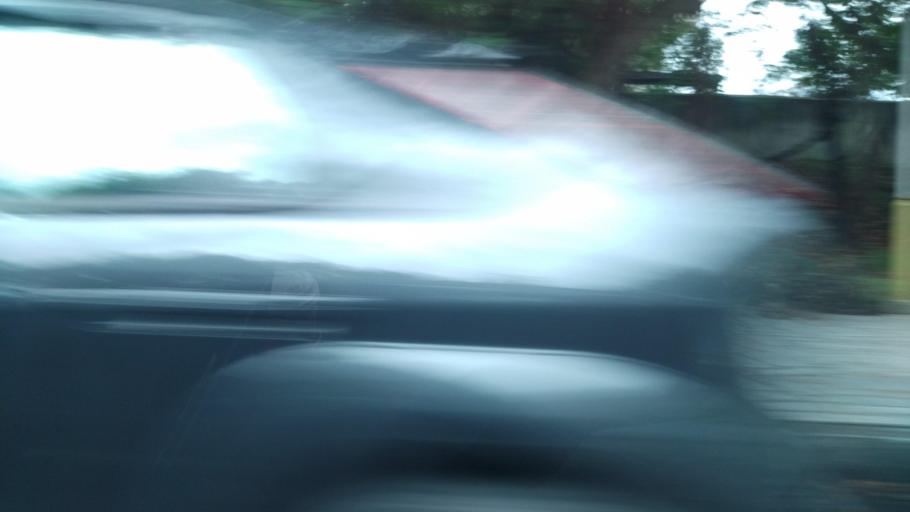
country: TW
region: Taiwan
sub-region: Hualien
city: Hualian
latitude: 24.0002
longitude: 121.6203
